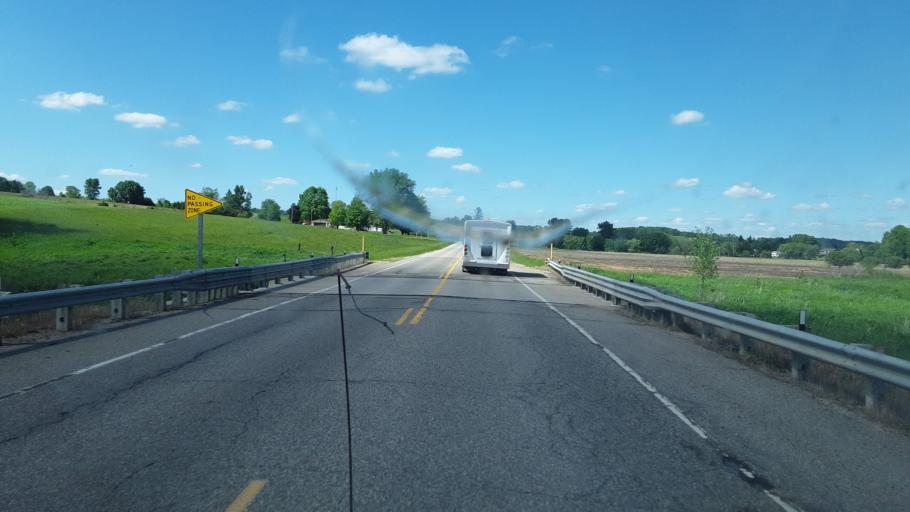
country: US
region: Wisconsin
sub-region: Vernon County
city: Hillsboro
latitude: 43.5121
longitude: -90.2068
